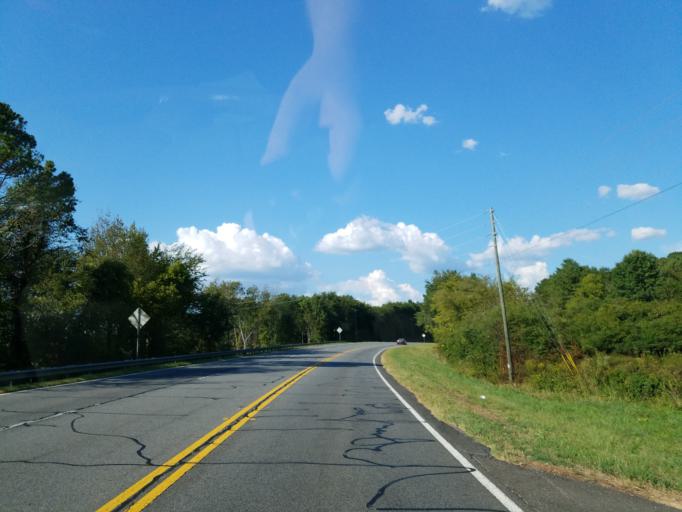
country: US
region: Georgia
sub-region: Bartow County
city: Rydal
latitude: 34.3808
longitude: -84.7094
